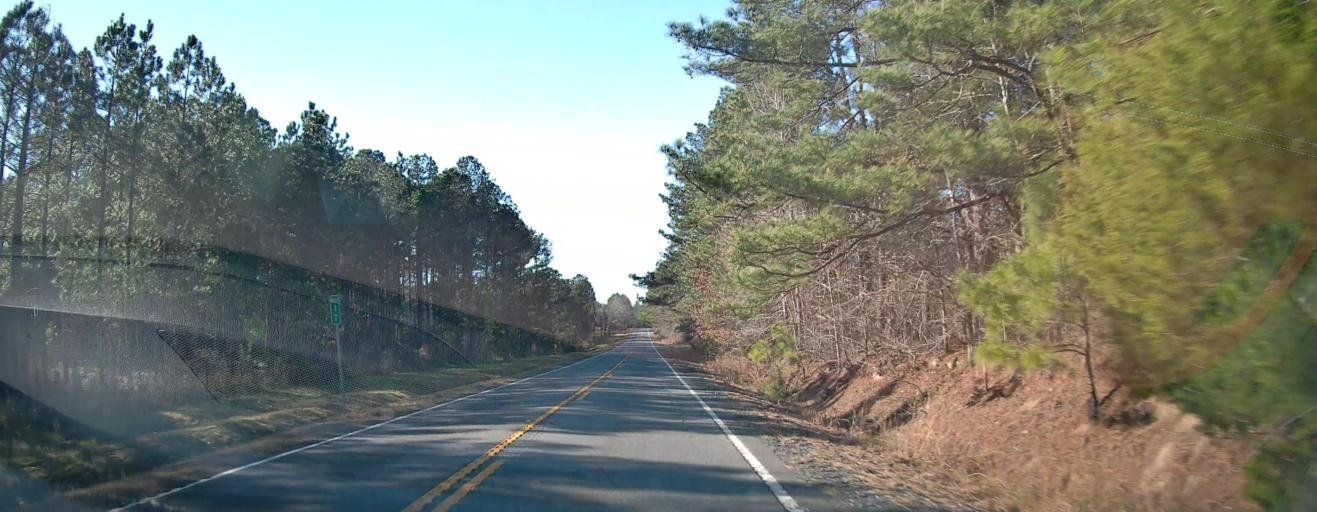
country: US
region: Georgia
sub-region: Talbot County
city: Talbotton
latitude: 32.6467
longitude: -84.4389
